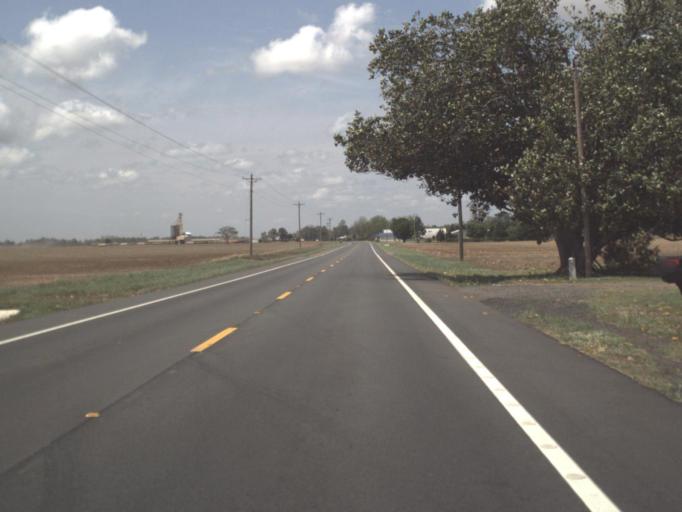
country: US
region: Florida
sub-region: Escambia County
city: Century
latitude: 30.8853
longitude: -87.1631
